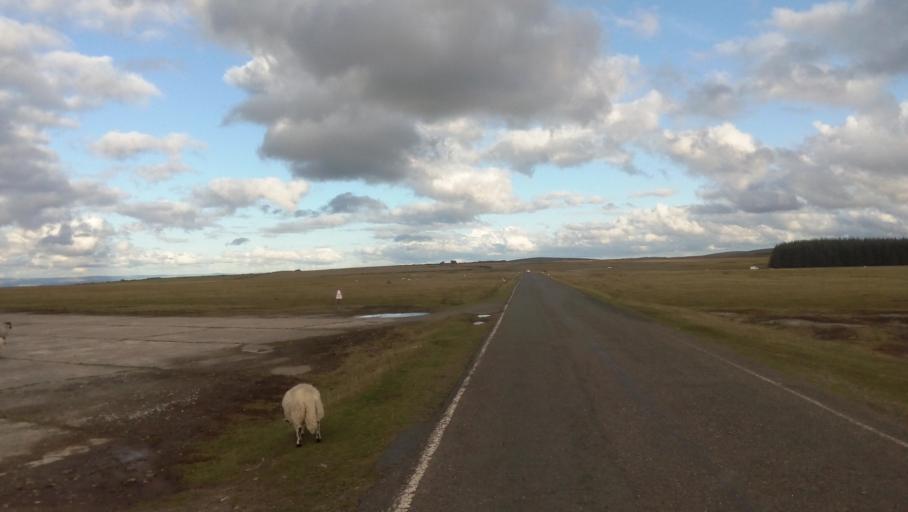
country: GB
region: England
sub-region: Cornwall
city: Camelford
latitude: 50.6351
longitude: -4.6167
